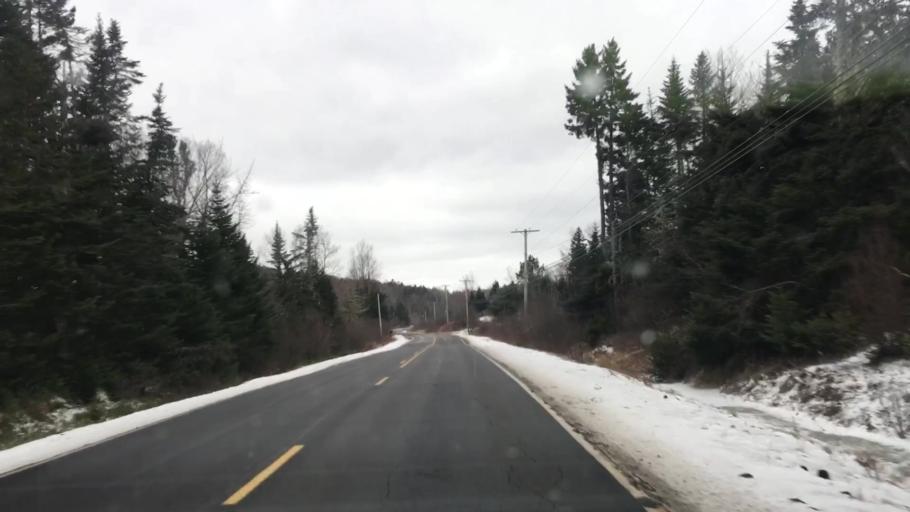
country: US
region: Maine
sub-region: Washington County
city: Machiasport
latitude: 44.7074
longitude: -67.3635
